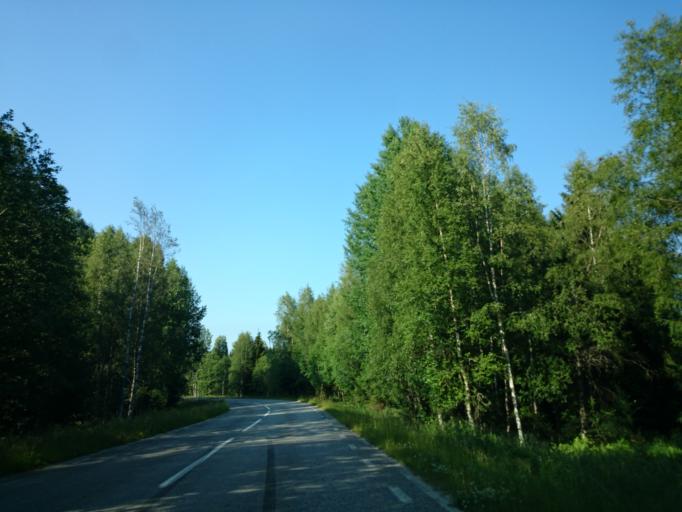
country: SE
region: Vaesternorrland
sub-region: Sundsvalls Kommun
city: Njurundabommen
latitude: 62.2115
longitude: 17.3760
